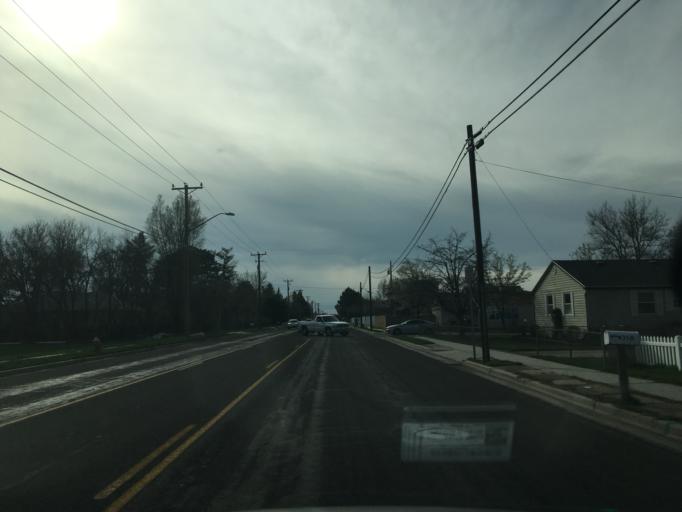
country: US
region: Utah
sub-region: Davis County
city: Layton
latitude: 41.0602
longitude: -111.9810
